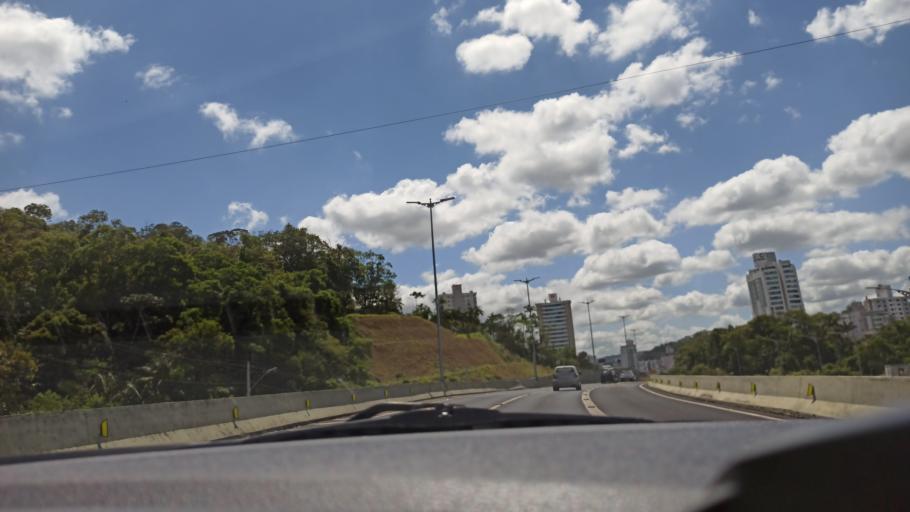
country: BR
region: Santa Catarina
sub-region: Blumenau
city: Blumenau
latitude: -26.9155
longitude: -49.0962
